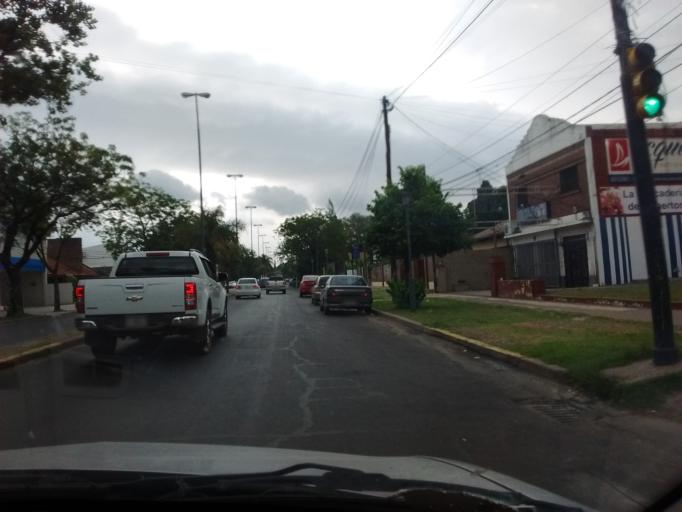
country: AR
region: Santa Fe
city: Granadero Baigorria
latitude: -32.9292
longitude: -60.7345
